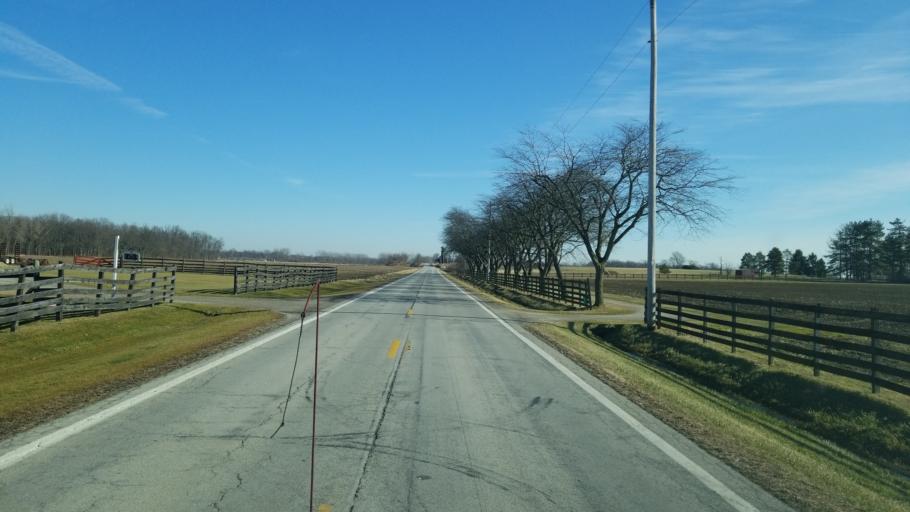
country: US
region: Ohio
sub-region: Henry County
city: Liberty Center
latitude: 41.4151
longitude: -83.9632
